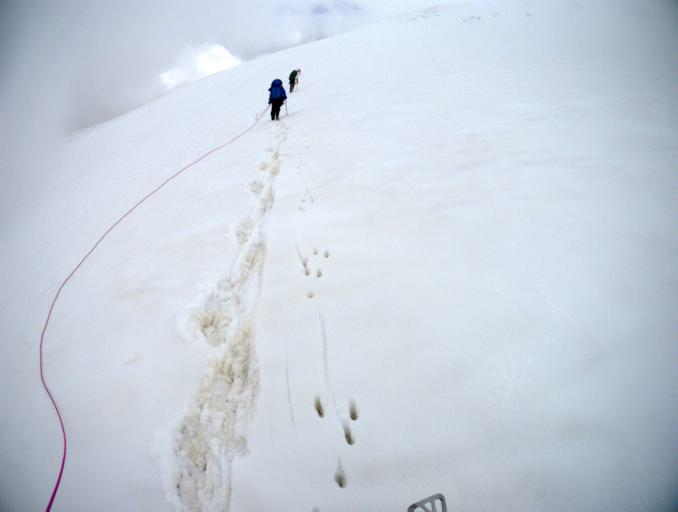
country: RU
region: Kabardino-Balkariya
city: Terskol
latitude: 43.3698
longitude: 42.4854
